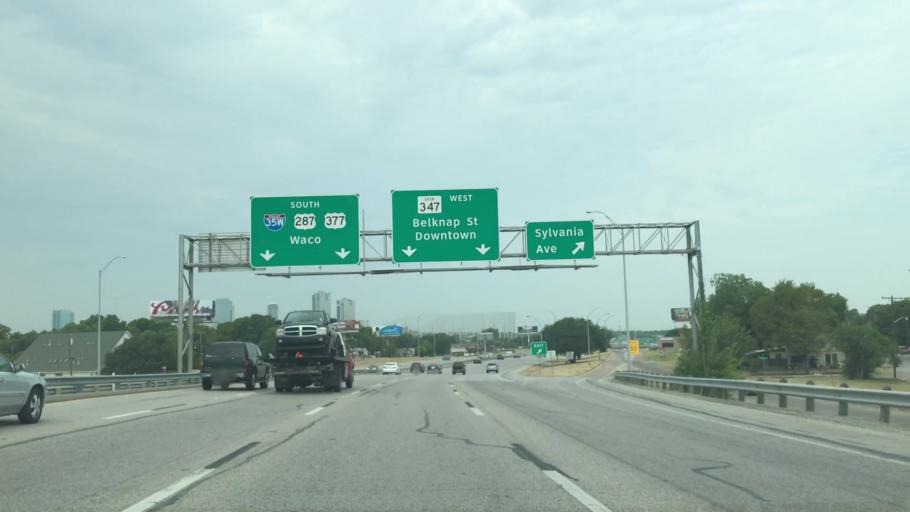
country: US
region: Texas
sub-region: Tarrant County
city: Haltom City
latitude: 32.7682
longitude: -97.3026
